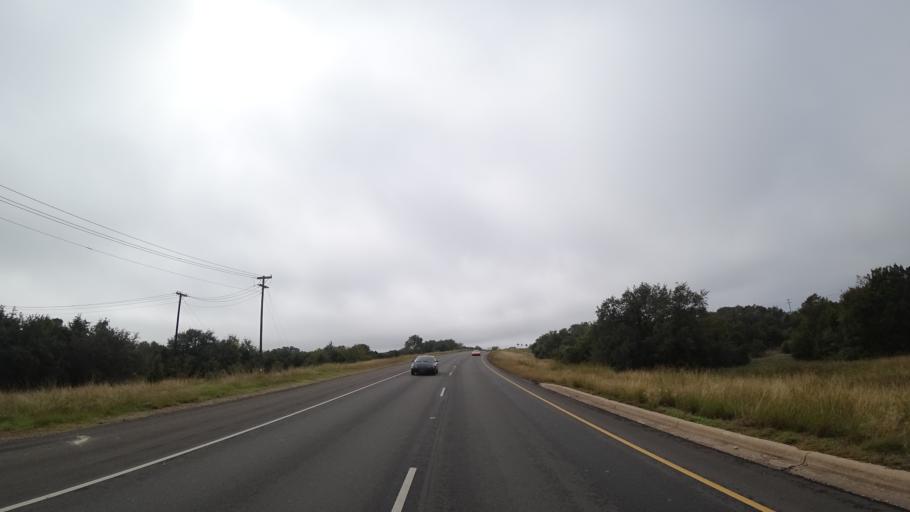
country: US
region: Texas
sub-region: Travis County
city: Shady Hollow
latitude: 30.1821
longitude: -97.8801
